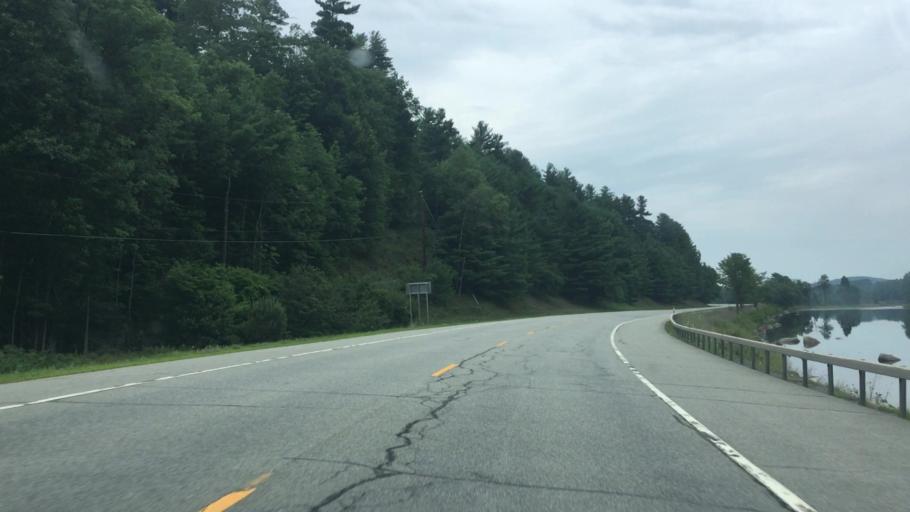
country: US
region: New York
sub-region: Essex County
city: Elizabethtown
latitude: 44.3534
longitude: -73.7541
